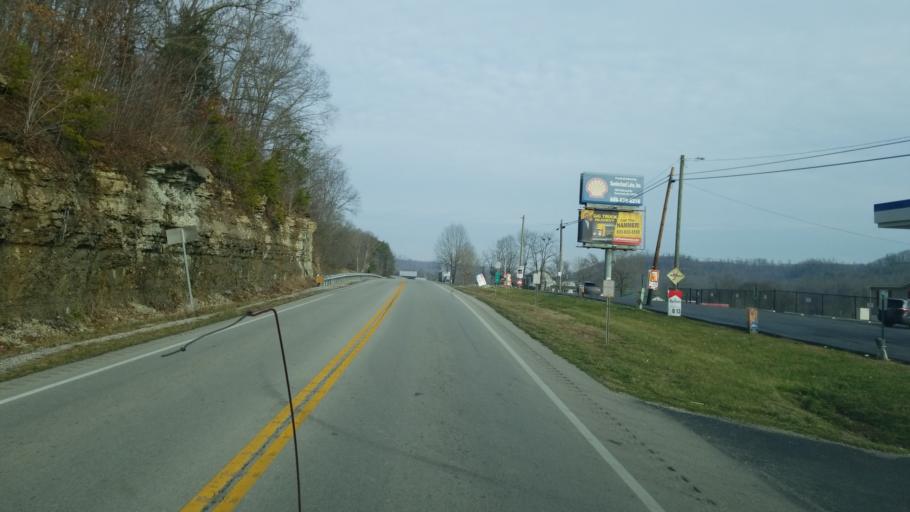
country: US
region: Kentucky
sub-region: Casey County
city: Liberty
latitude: 37.3611
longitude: -84.8673
